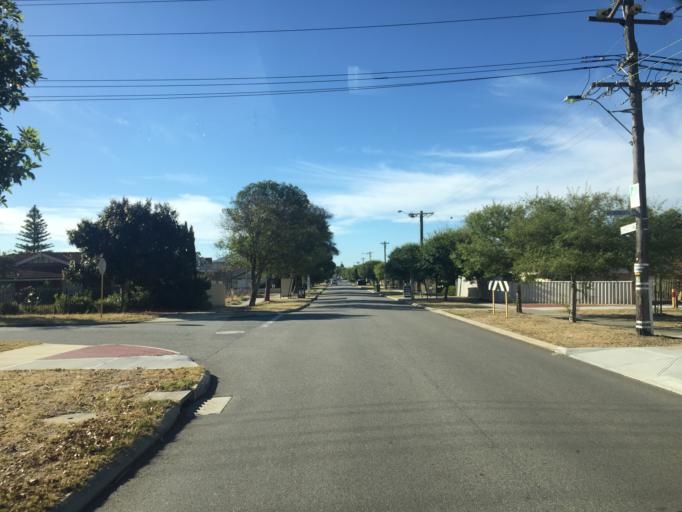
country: AU
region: Western Australia
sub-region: Belmont
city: Rivervale
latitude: -31.9661
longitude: 115.9189
